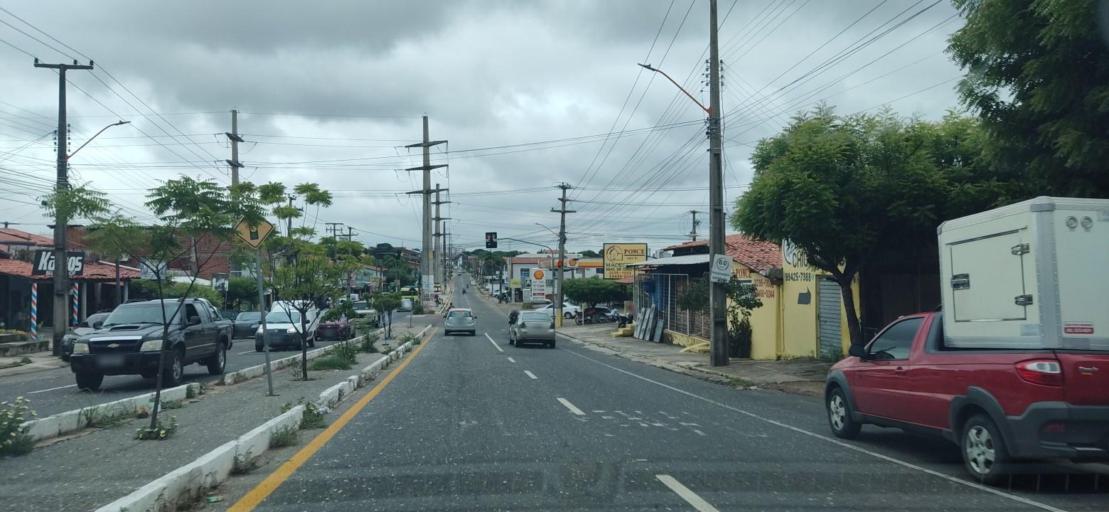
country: BR
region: Piaui
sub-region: Teresina
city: Teresina
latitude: -5.0581
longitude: -42.7509
